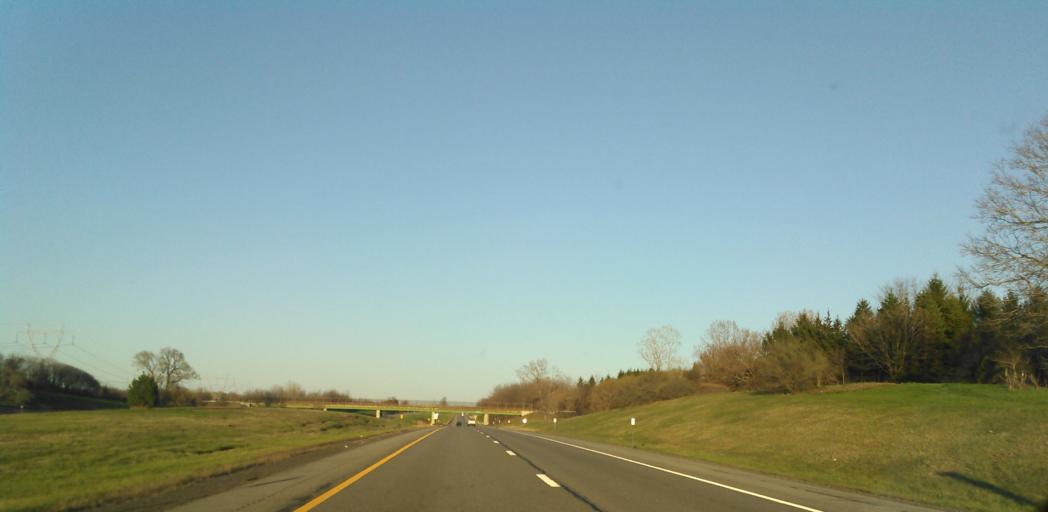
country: US
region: New York
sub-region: Monroe County
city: Honeoye Falls
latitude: 43.0470
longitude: -77.6035
